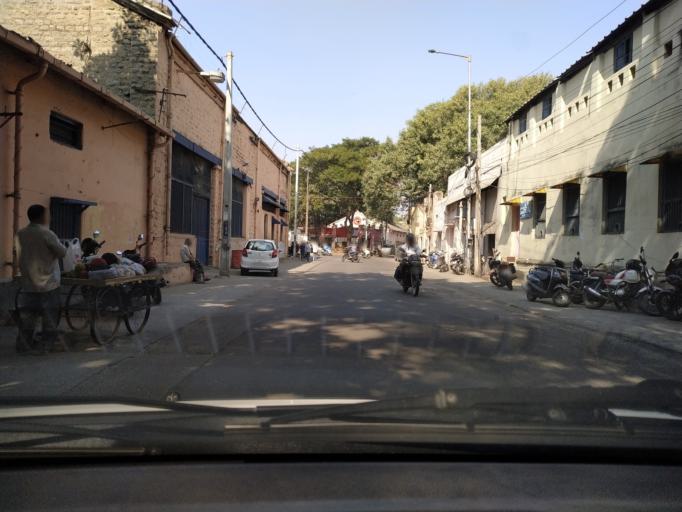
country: IN
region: Telangana
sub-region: Hyderabad
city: Hyderabad
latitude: 17.4099
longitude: 78.4676
